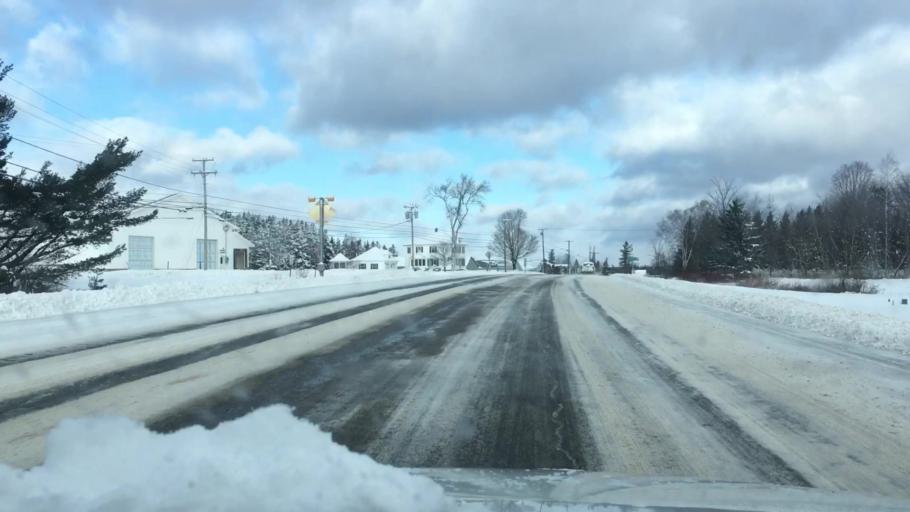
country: US
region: Maine
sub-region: Aroostook County
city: Caribou
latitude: 46.8805
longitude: -68.0118
